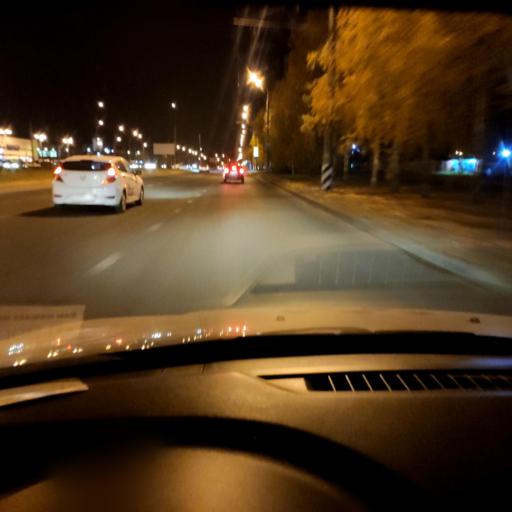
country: RU
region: Samara
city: Tol'yatti
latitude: 53.4985
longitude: 49.2847
